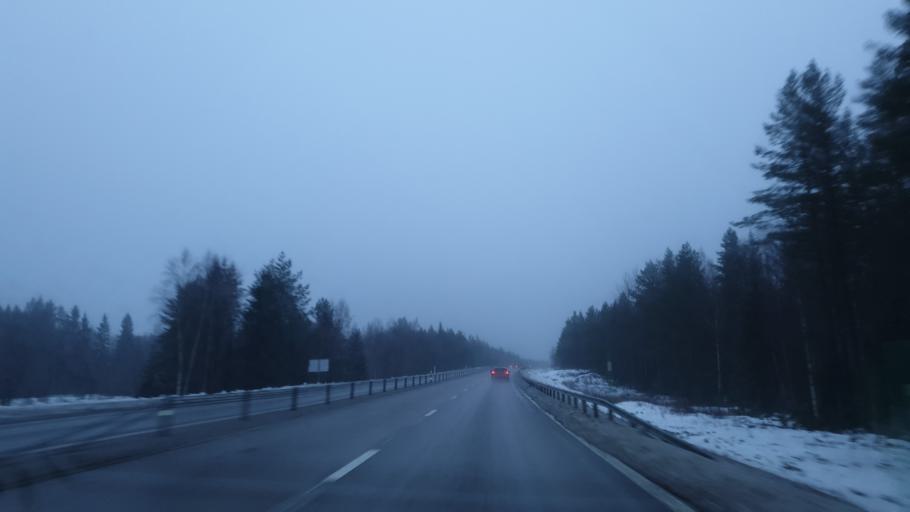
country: SE
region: Vaesterbotten
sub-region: Umea Kommun
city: Saevar
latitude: 63.9819
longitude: 20.7291
